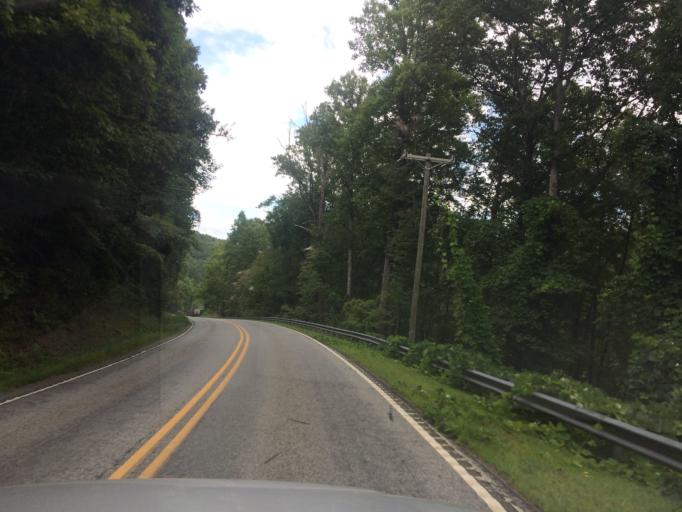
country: US
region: North Carolina
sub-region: Polk County
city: Columbus
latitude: 35.3253
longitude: -82.1836
